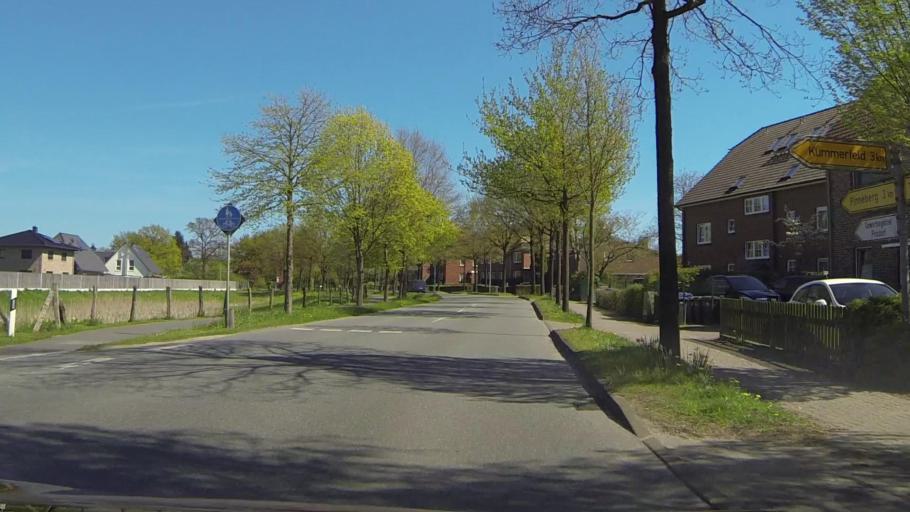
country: DE
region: Schleswig-Holstein
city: Prisdorf
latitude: 53.6779
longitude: 9.7637
